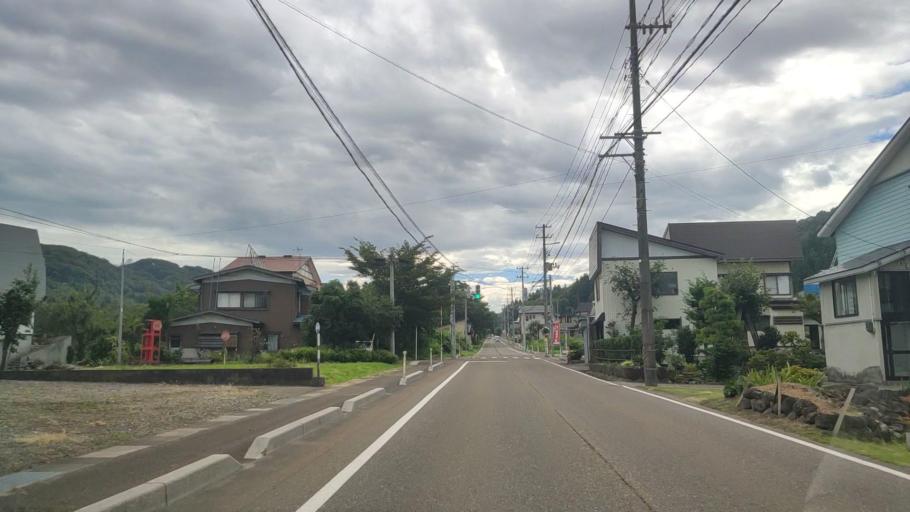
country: JP
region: Niigata
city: Arai
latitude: 37.0014
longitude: 138.2647
